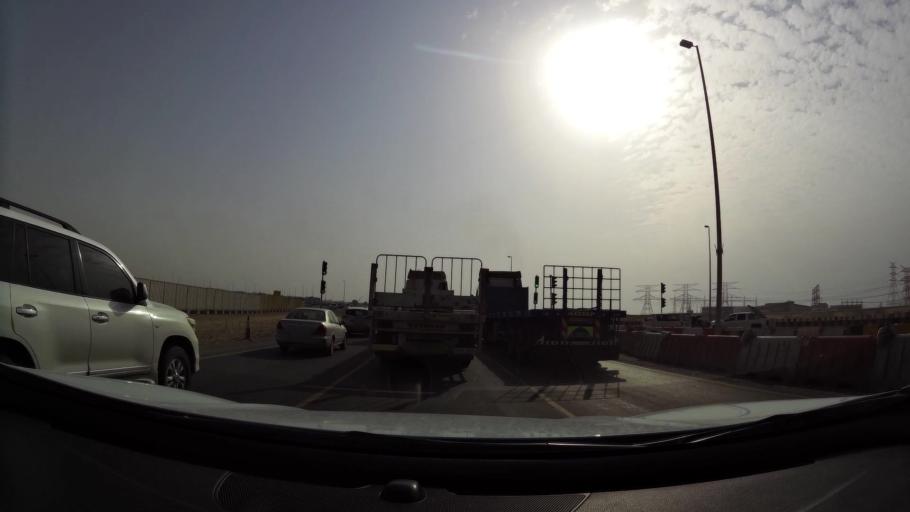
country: AE
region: Abu Dhabi
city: Abu Dhabi
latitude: 24.2917
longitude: 54.5468
